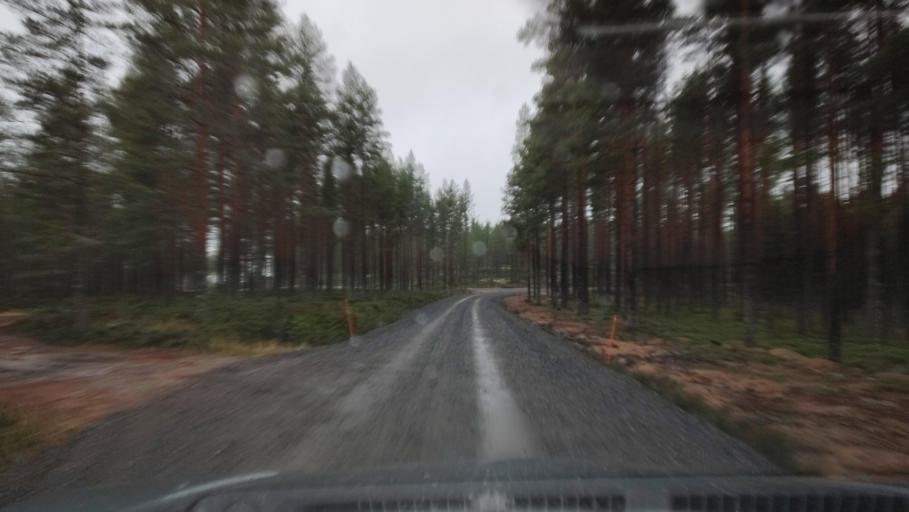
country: FI
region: Southern Ostrobothnia
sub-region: Suupohja
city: Karijoki
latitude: 62.1491
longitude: 21.6210
